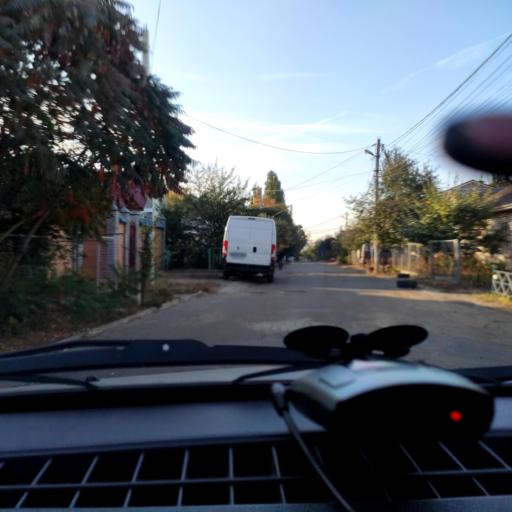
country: RU
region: Voronezj
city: Podgornoye
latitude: 51.7002
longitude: 39.1541
